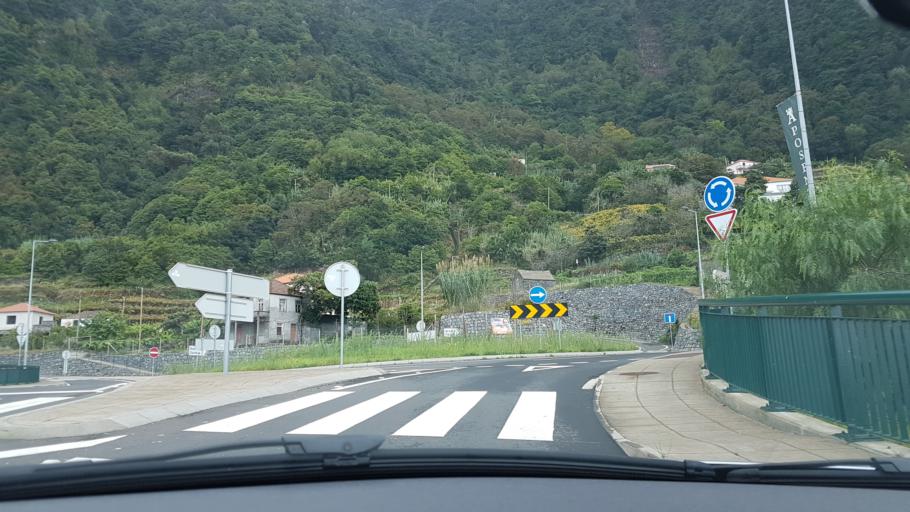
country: PT
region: Madeira
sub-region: Sao Vicente
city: Sao Vicente
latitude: 32.8219
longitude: -16.9905
